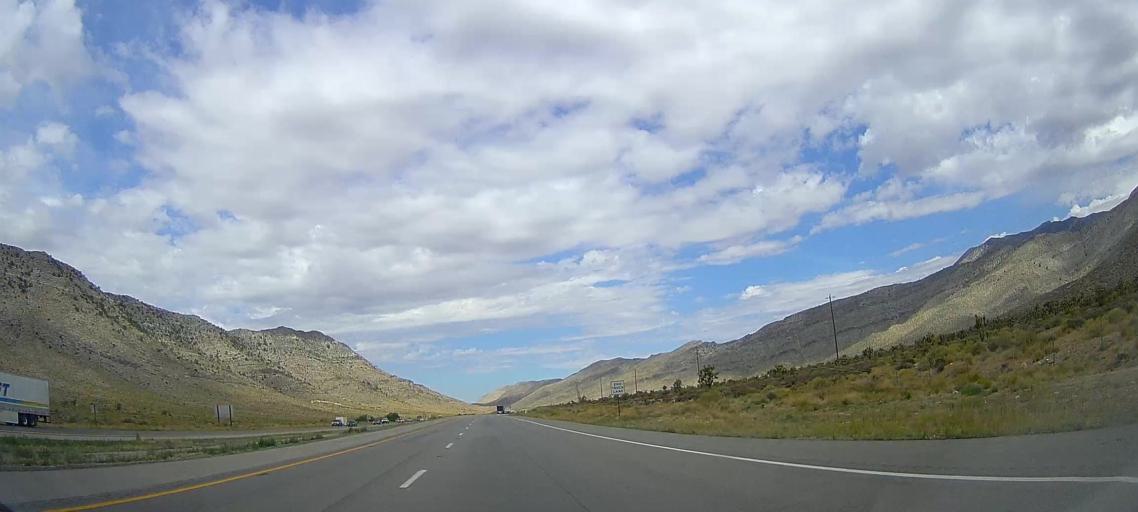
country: US
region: Nevada
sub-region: Clark County
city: Sandy Valley
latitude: 35.4709
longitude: -115.5513
